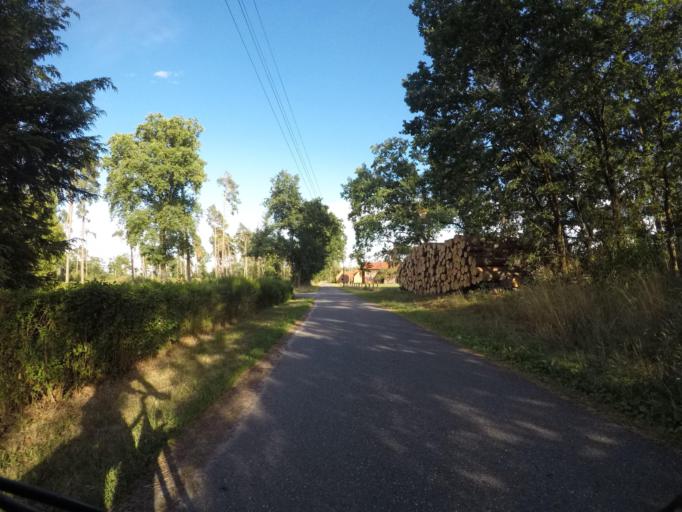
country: DE
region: Mecklenburg-Vorpommern
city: Lubtheen
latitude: 53.2346
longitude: 11.0420
